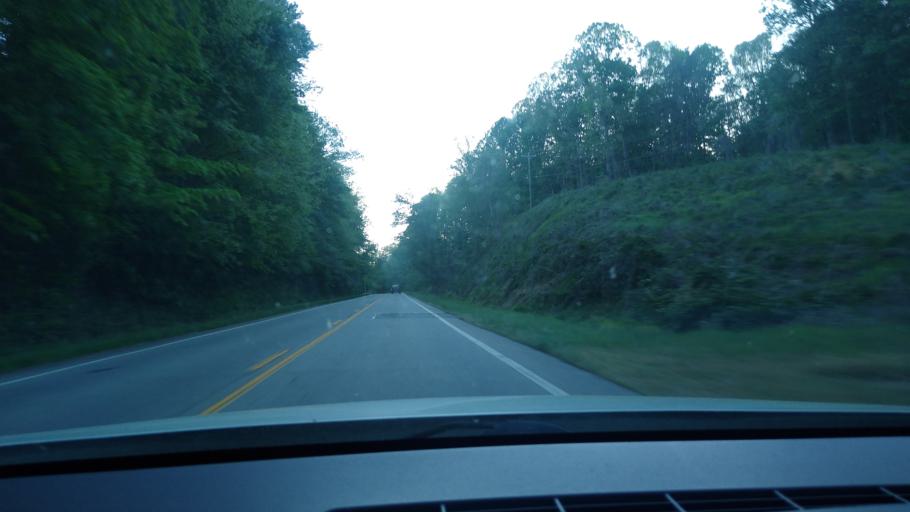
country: US
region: North Carolina
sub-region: Rockingham County
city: Reidsville
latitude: 36.3984
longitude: -79.5330
